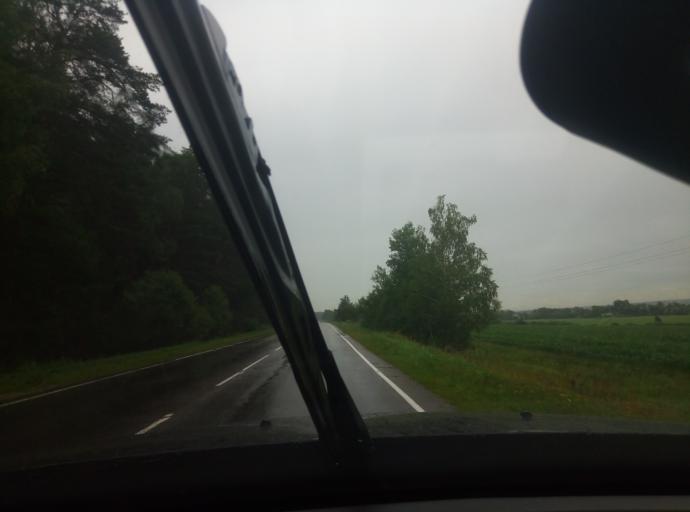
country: RU
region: Kaluga
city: Kremenki
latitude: 54.8914
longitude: 37.0672
